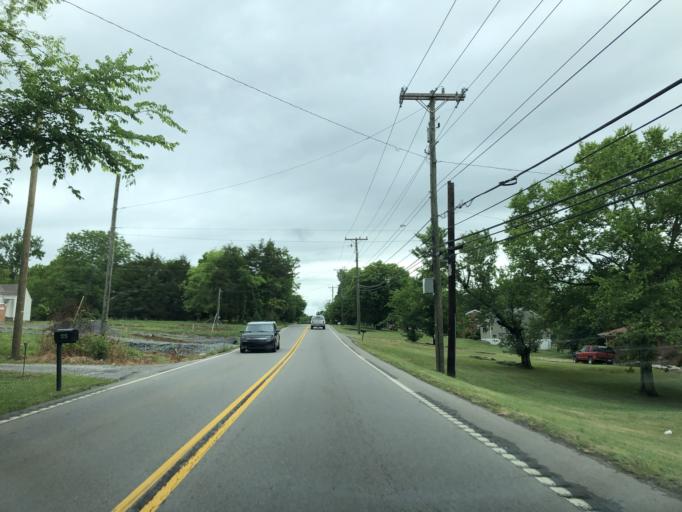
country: US
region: Tennessee
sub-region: Davidson County
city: Goodlettsville
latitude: 36.2725
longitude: -86.7622
